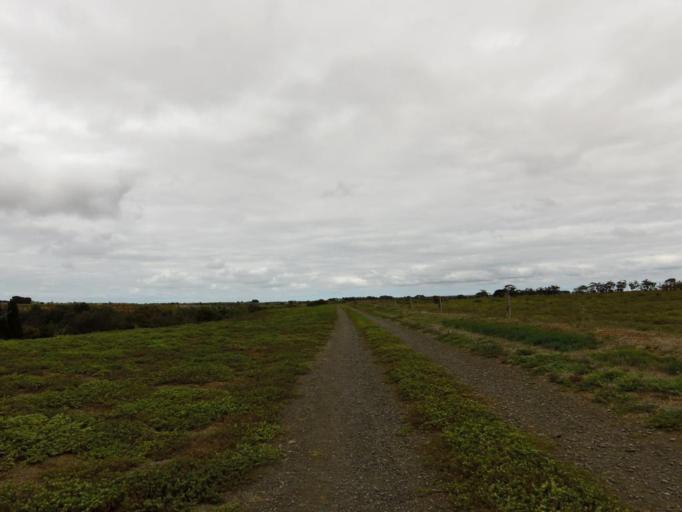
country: AU
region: Victoria
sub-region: Wyndham
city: Werribee
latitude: -37.9435
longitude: 144.6652
